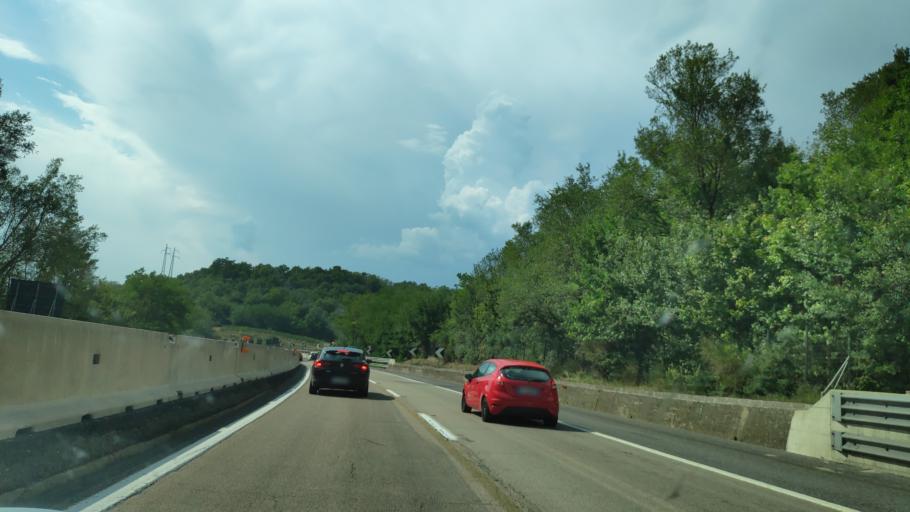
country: IT
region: Tuscany
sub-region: Province of Arezzo
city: Montalto
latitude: 43.5147
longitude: 11.6360
